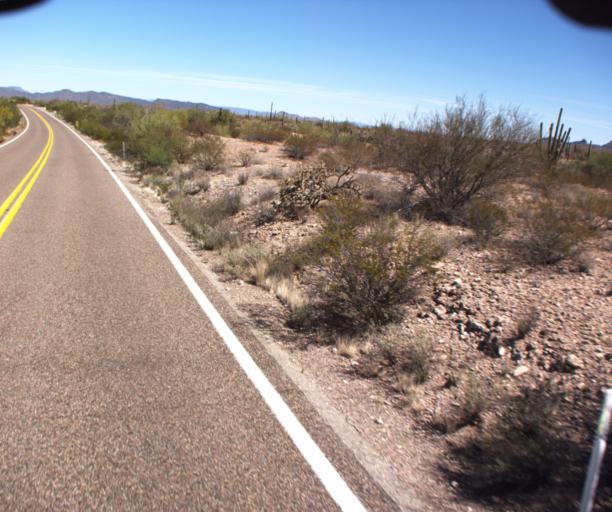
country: MX
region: Sonora
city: Sonoyta
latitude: 32.0988
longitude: -112.7718
